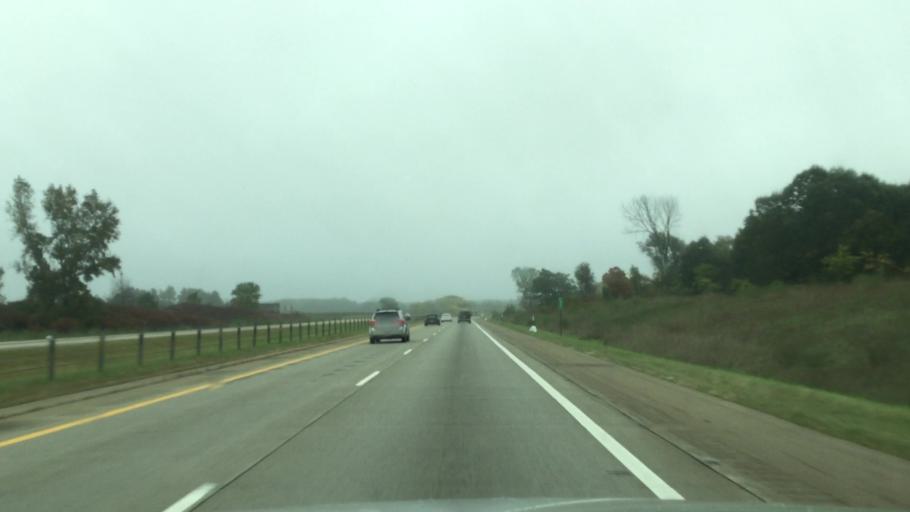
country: US
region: Michigan
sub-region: Van Buren County
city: Paw Paw
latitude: 42.2027
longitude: -85.9540
